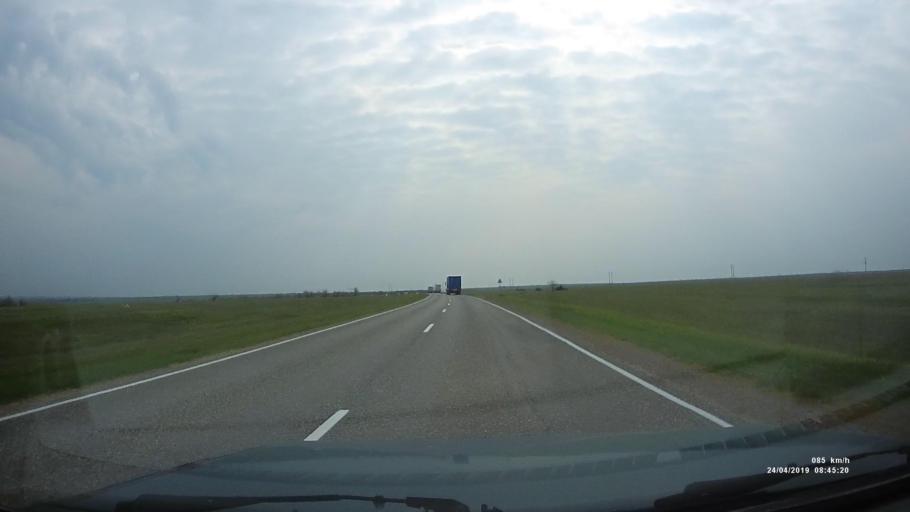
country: RU
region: Kalmykiya
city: Arshan'
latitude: 46.2363
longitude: 44.0589
